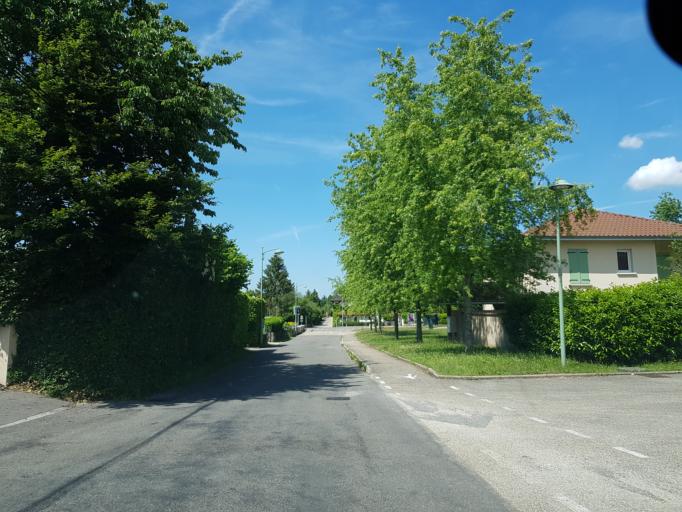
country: FR
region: Rhone-Alpes
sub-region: Departement de l'Ain
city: Montagnat
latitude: 46.1912
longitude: 5.2792
